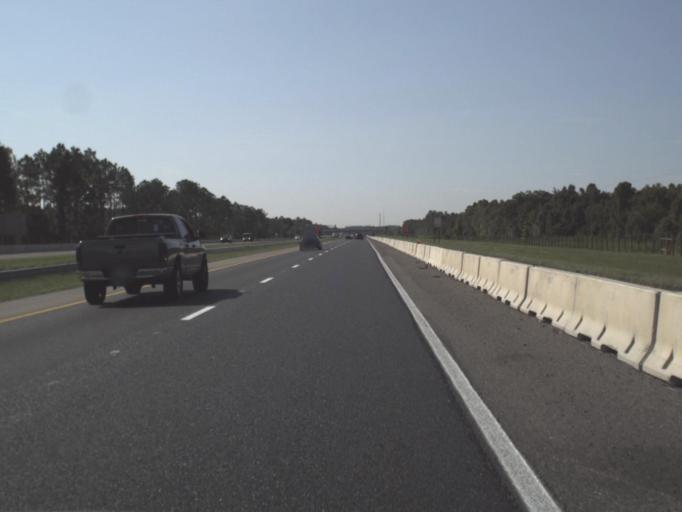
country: US
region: Florida
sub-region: Hillsborough County
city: Pebble Creek
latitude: 28.1560
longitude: -82.3918
